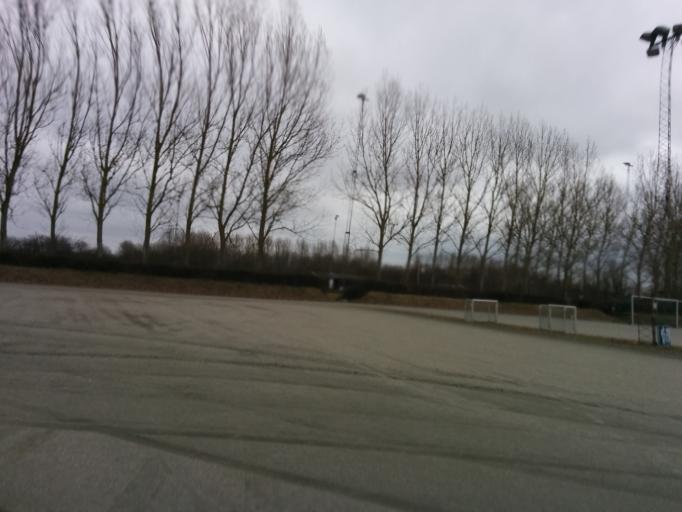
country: DK
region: Capital Region
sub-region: Ballerup Kommune
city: Ballerup
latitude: 55.7176
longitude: 12.3709
